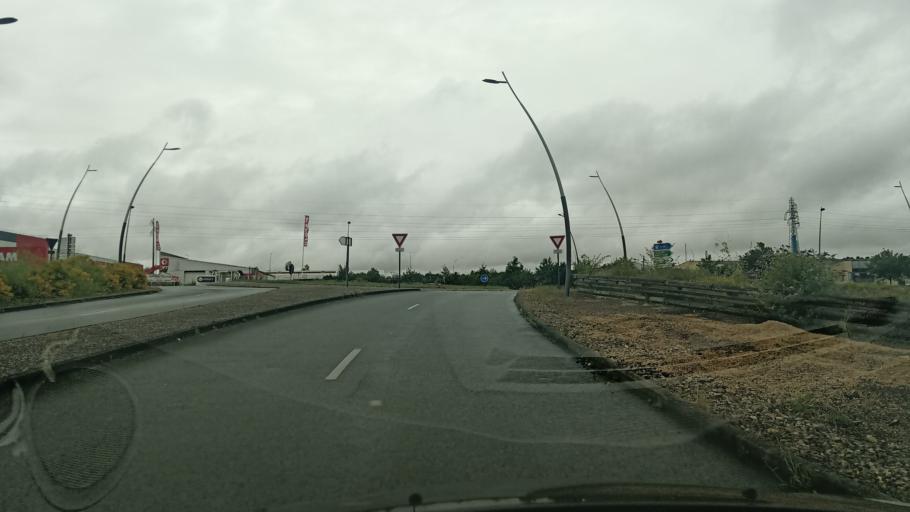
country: FR
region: Poitou-Charentes
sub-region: Departement de la Vienne
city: Poitiers
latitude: 46.6128
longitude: 0.3483
